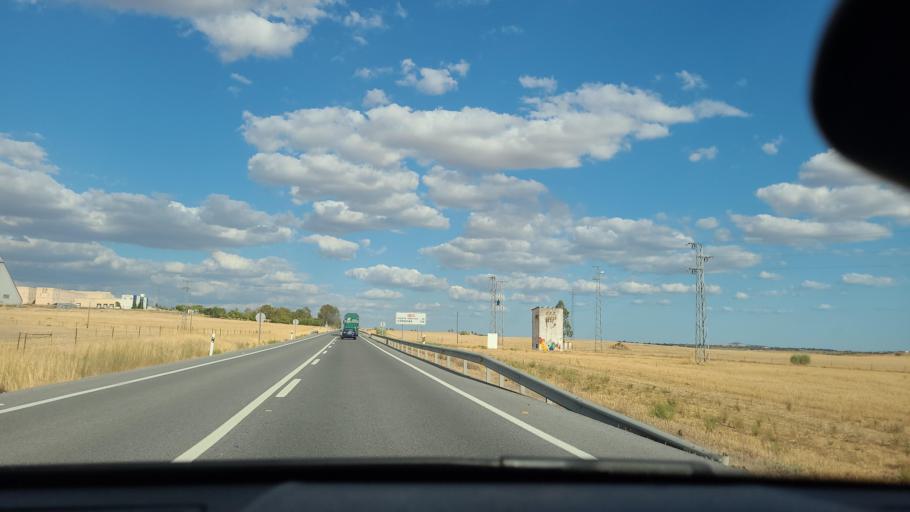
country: ES
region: Extremadura
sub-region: Provincia de Badajoz
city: Granja de Torrehermosa
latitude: 38.3023
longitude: -5.6106
